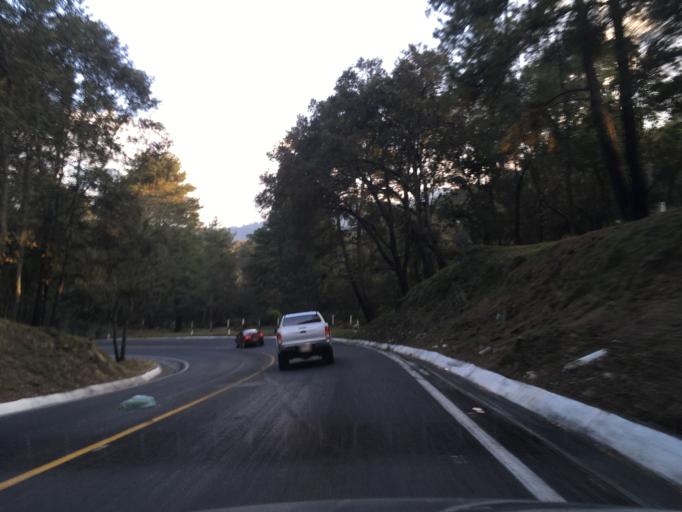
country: MX
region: Michoacan
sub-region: Patzcuaro
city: Santa Maria Huiramangaro (San Juan Tumbio)
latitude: 19.4972
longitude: -101.7117
